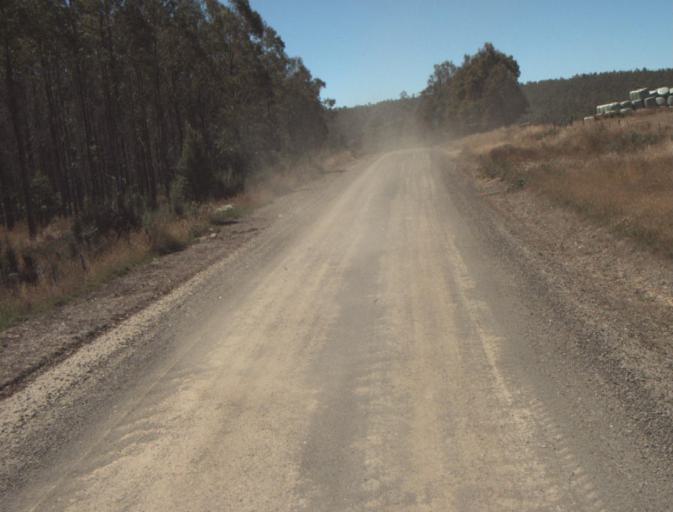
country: AU
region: Tasmania
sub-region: Dorset
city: Scottsdale
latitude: -41.3249
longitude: 147.4450
